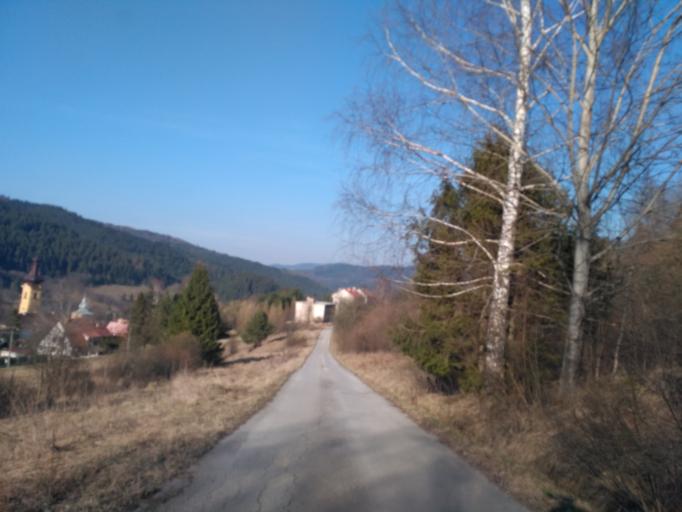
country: SK
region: Kosicky
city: Medzev
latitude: 48.7258
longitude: 20.7375
